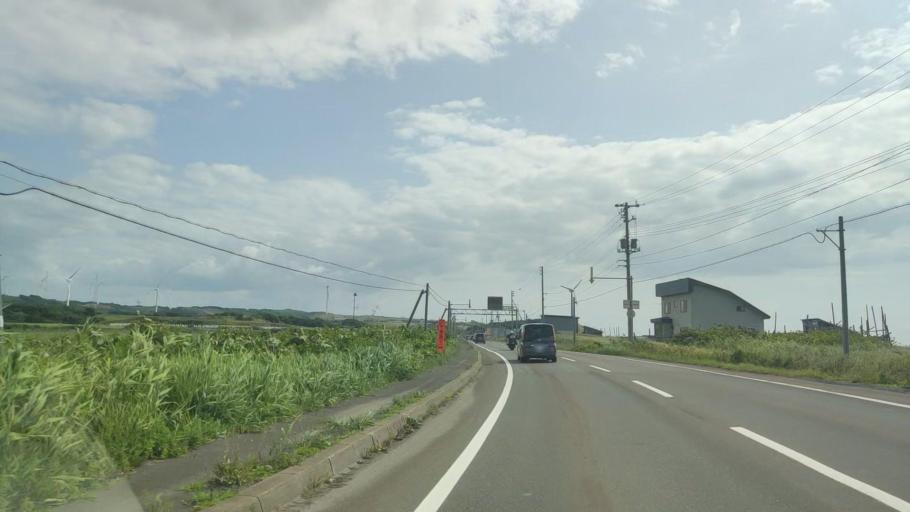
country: JP
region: Hokkaido
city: Rumoi
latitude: 44.2678
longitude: 141.6550
